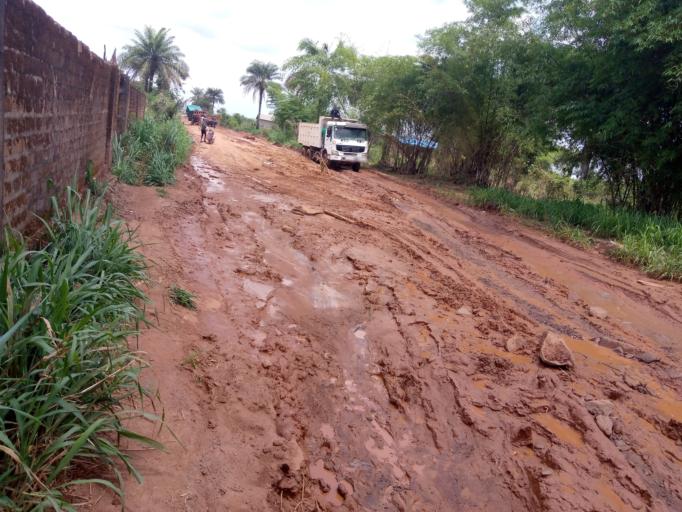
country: SL
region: Western Area
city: Waterloo
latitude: 8.3879
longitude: -12.9511
